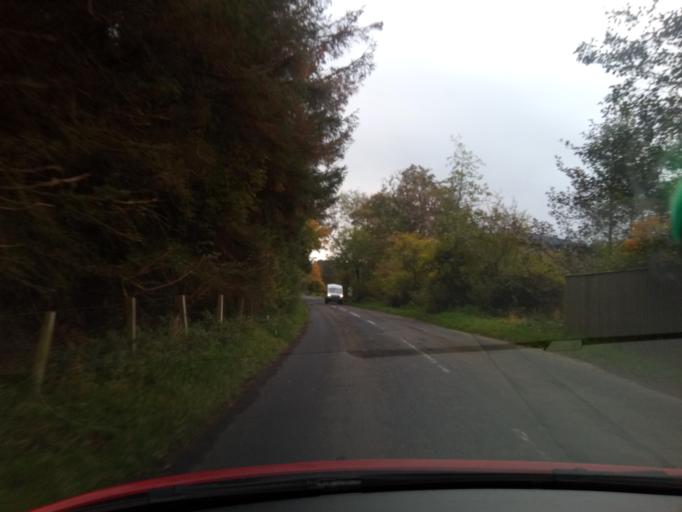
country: GB
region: Scotland
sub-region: The Scottish Borders
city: Galashiels
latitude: 55.6160
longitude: -2.8769
